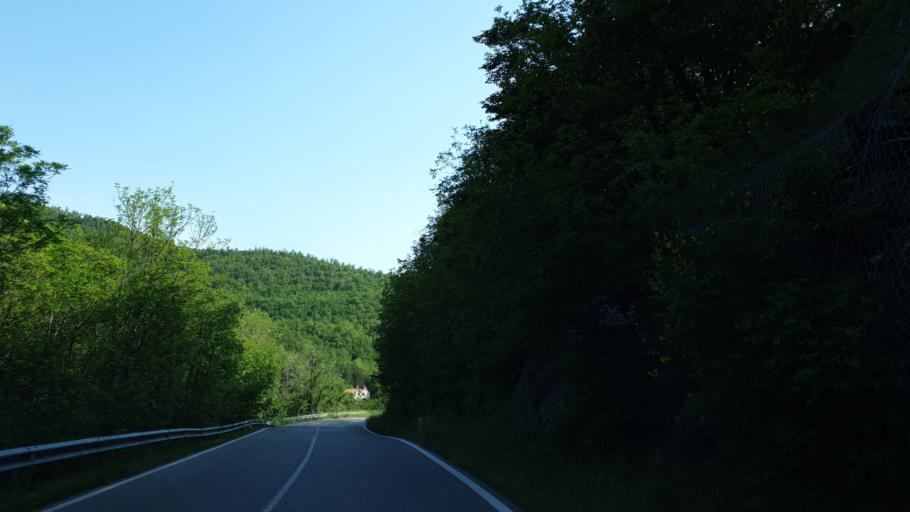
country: IT
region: Tuscany
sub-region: Province of Arezzo
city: Soci
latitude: 43.7623
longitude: 11.8353
